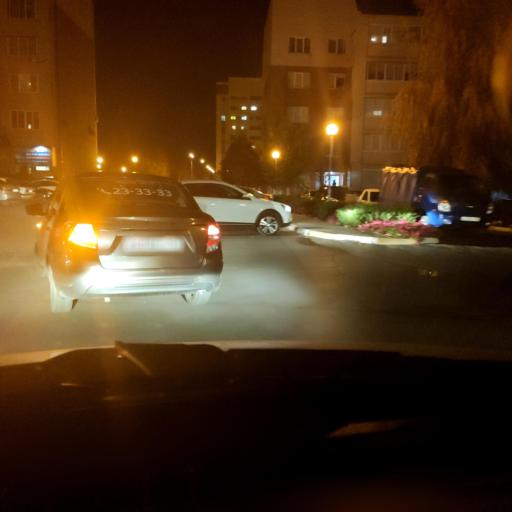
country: RU
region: Samara
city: Tol'yatti
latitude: 53.5462
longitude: 49.3162
